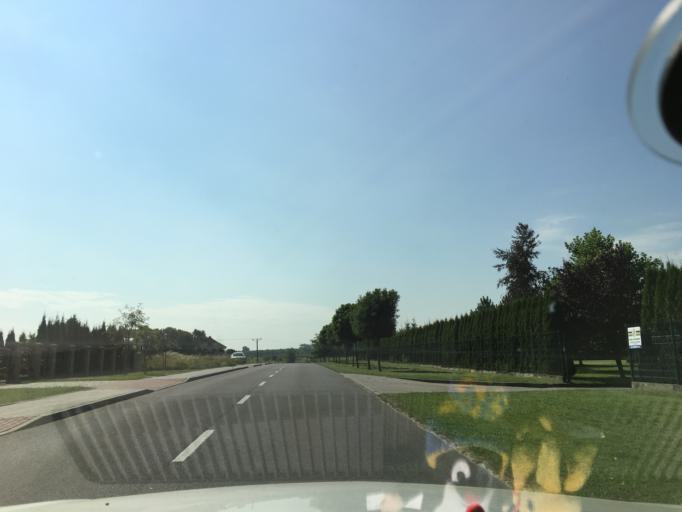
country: PL
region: West Pomeranian Voivodeship
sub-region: Powiat gryficki
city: Pobierowo
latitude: 54.0395
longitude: 14.8738
